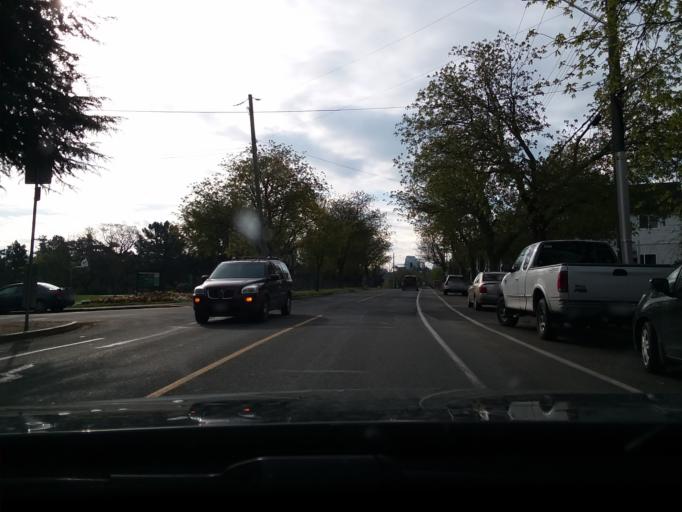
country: CA
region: British Columbia
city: Victoria
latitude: 48.4383
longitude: -123.3899
